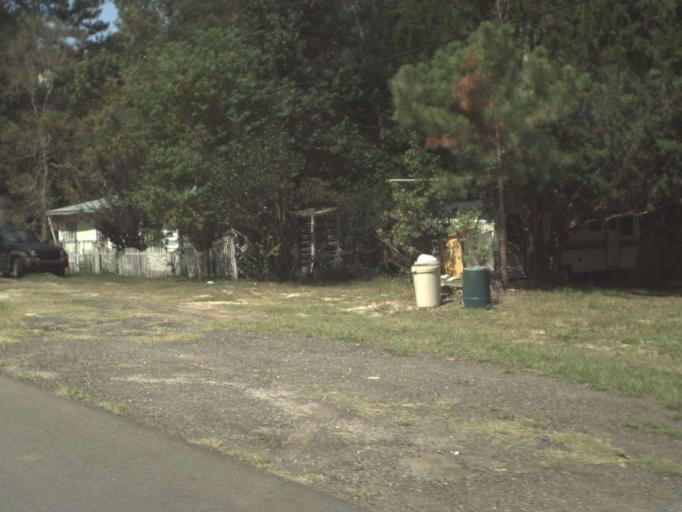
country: US
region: Florida
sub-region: Walton County
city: Freeport
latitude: 30.5040
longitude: -86.1525
